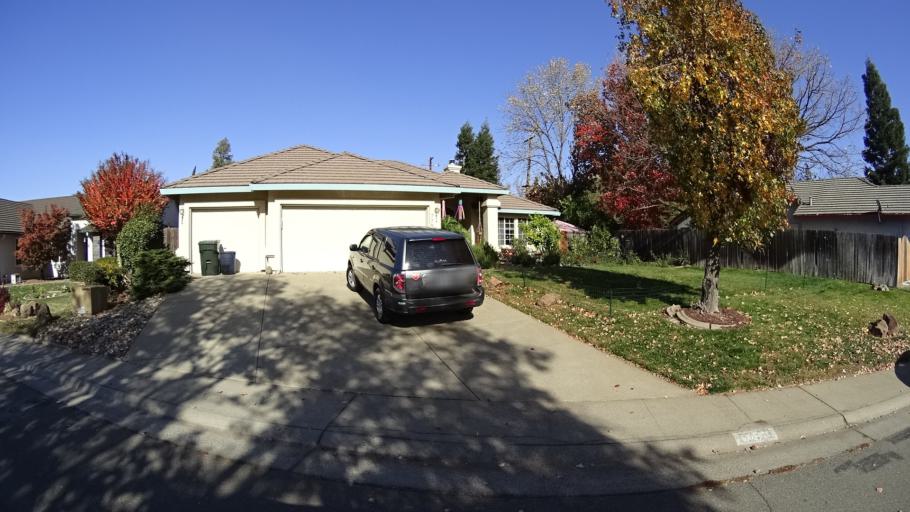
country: US
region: California
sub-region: Sacramento County
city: Citrus Heights
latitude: 38.7036
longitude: -121.2783
